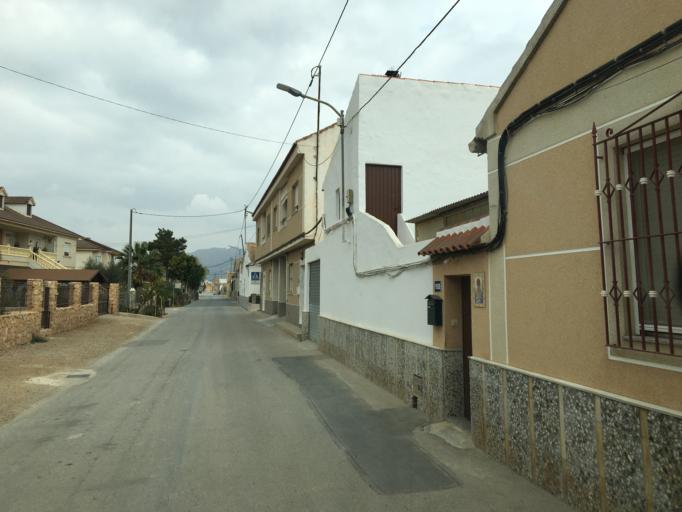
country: ES
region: Murcia
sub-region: Murcia
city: Beniel
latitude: 38.0353
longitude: -0.9855
